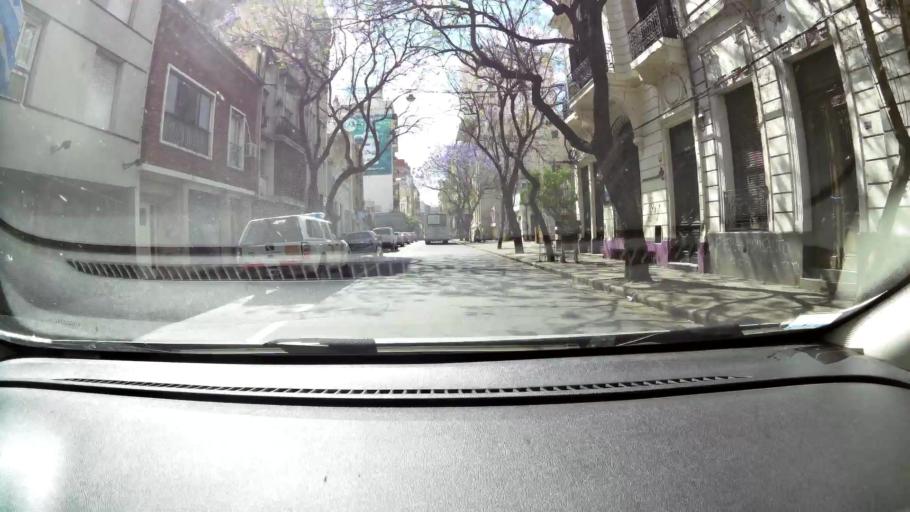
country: AR
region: Santa Fe
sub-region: Departamento de Rosario
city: Rosario
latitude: -32.9434
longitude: -60.6426
